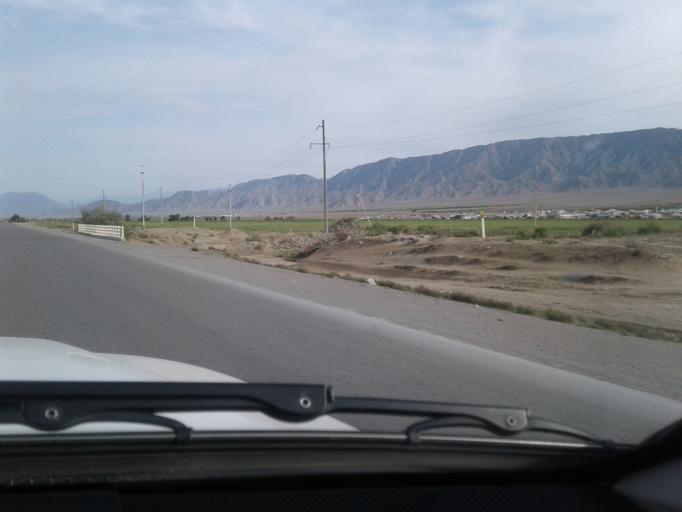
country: TM
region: Ahal
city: Arcabil
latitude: 38.2095
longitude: 57.8146
